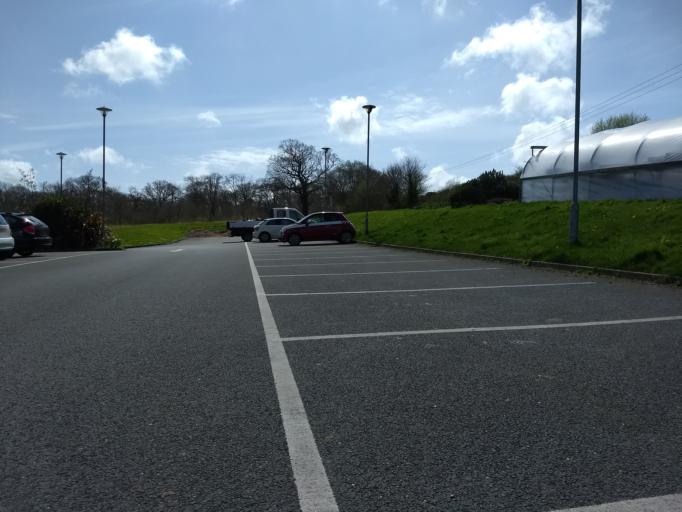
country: GB
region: England
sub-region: Isle of Wight
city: Newchurch
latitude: 50.7229
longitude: -1.2284
